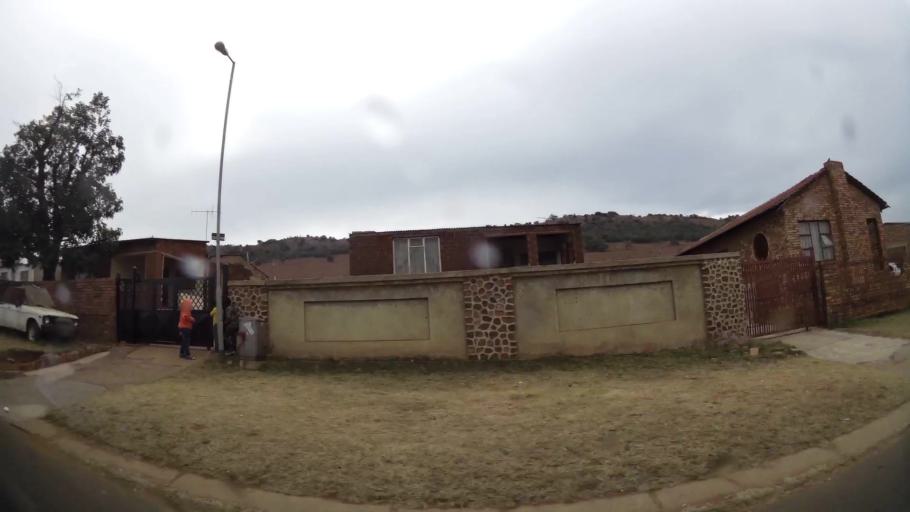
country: ZA
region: Gauteng
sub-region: City of Tshwane Metropolitan Municipality
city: Pretoria
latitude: -25.7022
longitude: 28.3487
